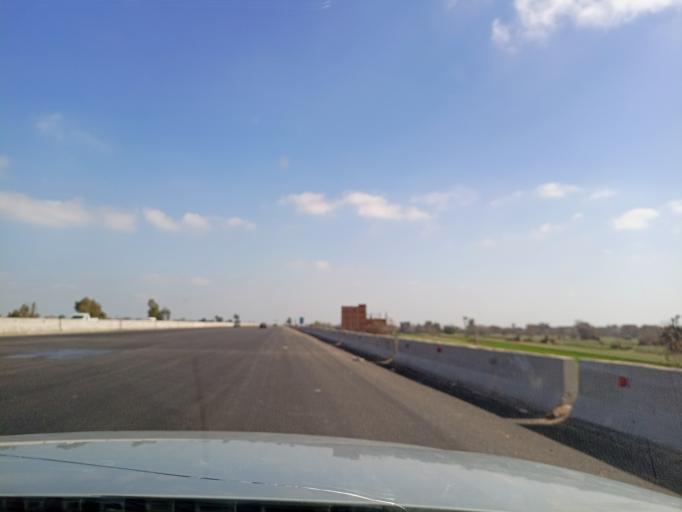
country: EG
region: Muhafazat al Minufiyah
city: Al Bajur
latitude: 30.4096
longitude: 31.0538
